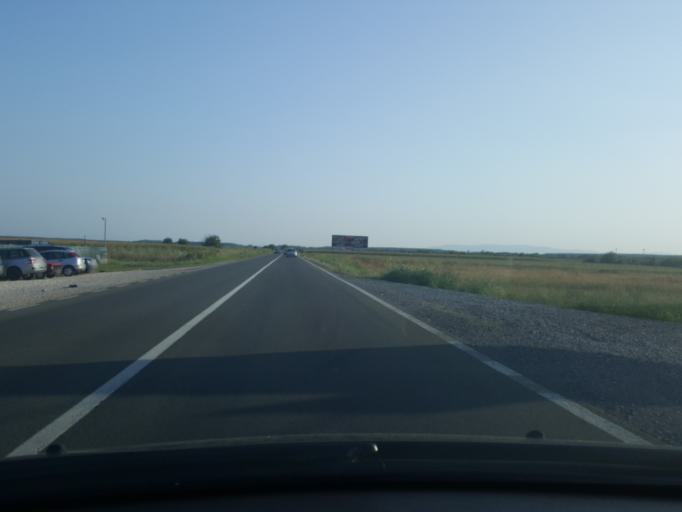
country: RS
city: Klenak
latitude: 44.7976
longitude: 19.7285
